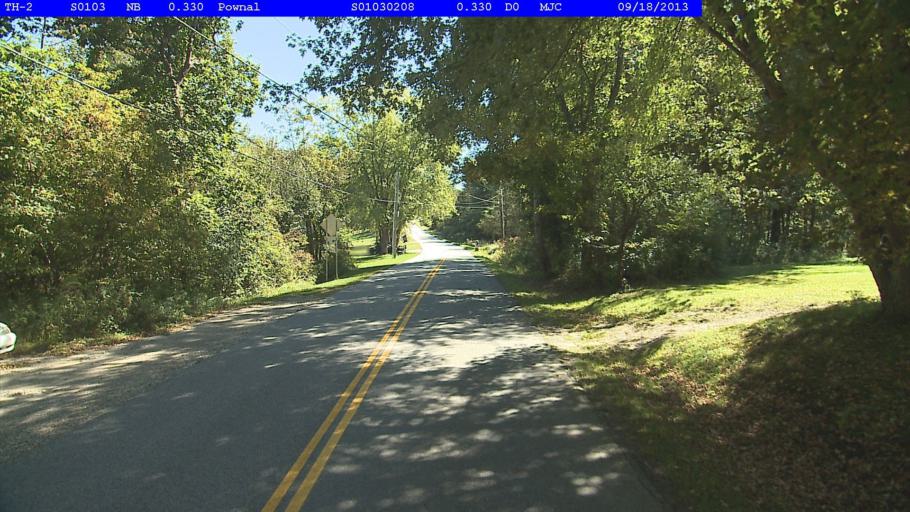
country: US
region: Vermont
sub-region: Bennington County
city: Bennington
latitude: 42.8066
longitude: -73.2613
